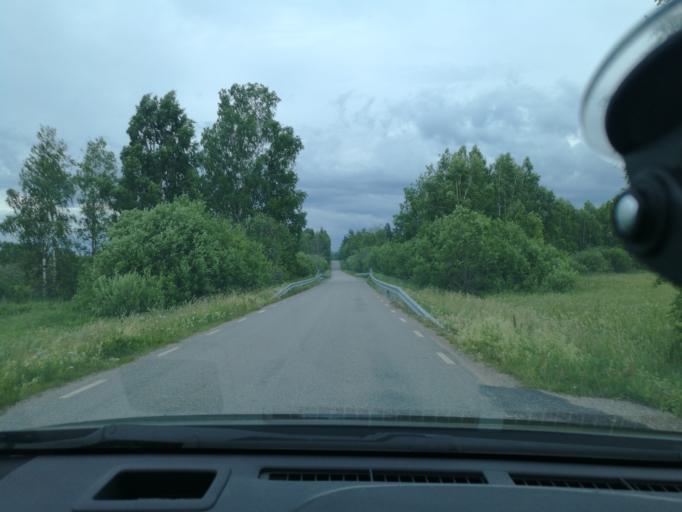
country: SE
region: Vaestmanland
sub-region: Vasteras
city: Skultuna
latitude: 59.8808
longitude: 16.3529
